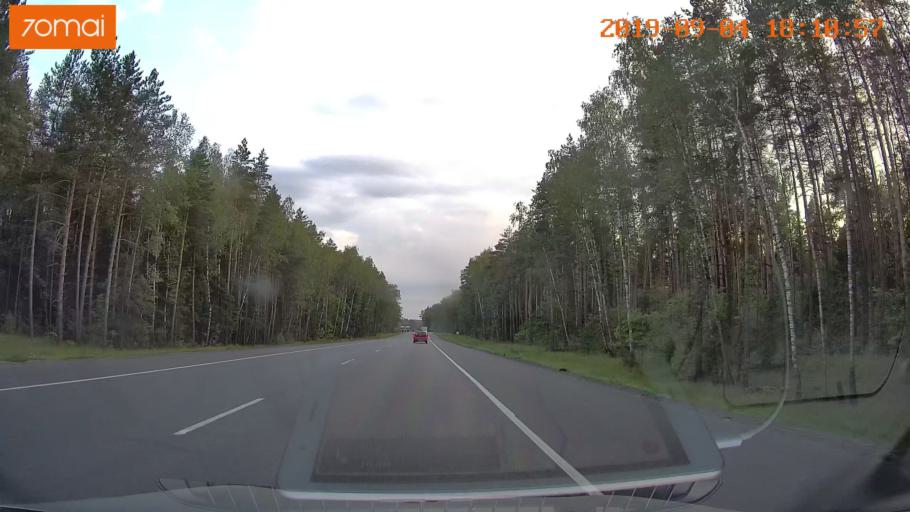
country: RU
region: Moskovskaya
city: Lopatinskiy
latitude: 55.3827
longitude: 38.7596
